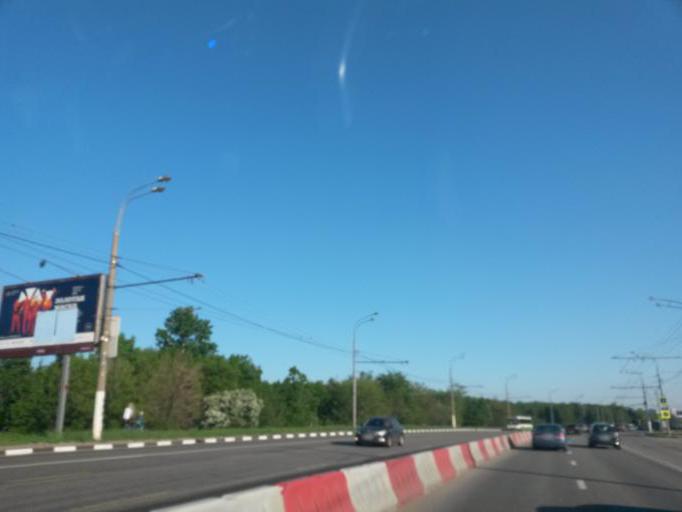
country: RU
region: Moscow
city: Orekhovo-Borisovo Severnoye
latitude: 55.6041
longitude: 37.6697
